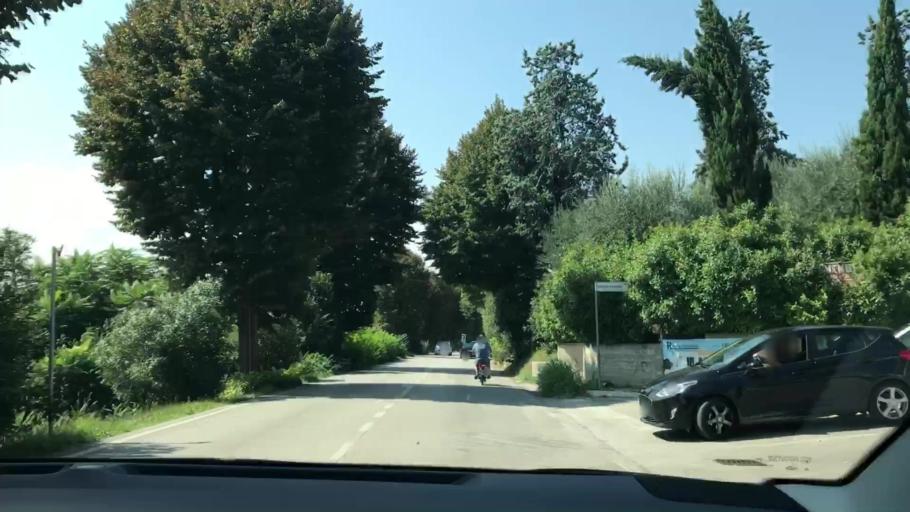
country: IT
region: The Marches
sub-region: Provincia di Ascoli Piceno
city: San Benedetto del Tronto
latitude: 42.9101
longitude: 13.8839
